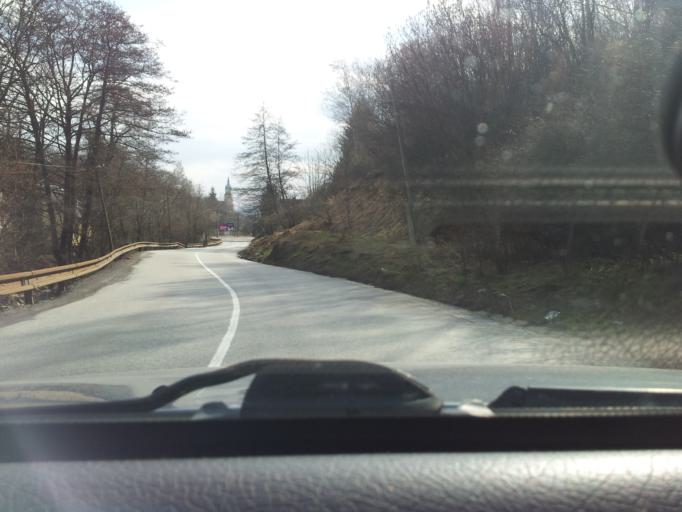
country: SK
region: Banskobystricky
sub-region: Okres Ziar nad Hronom
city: Kremnica
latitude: 48.7138
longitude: 18.9178
